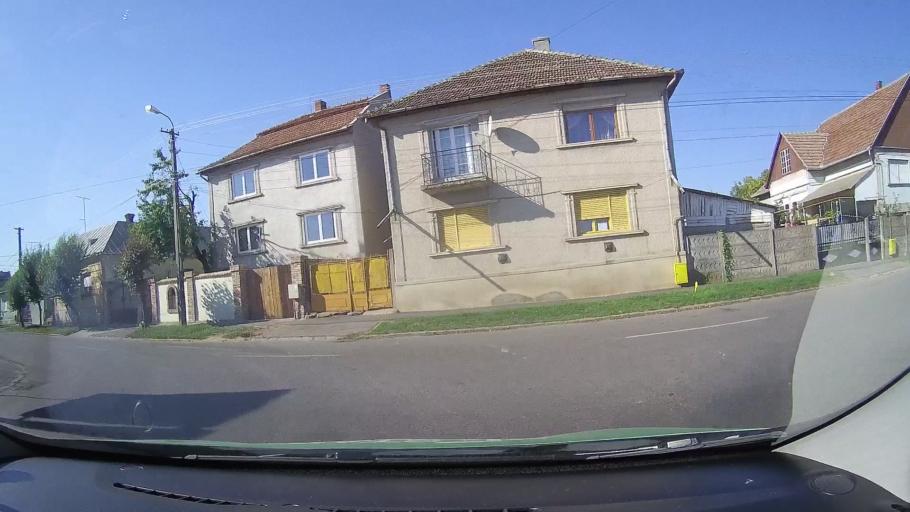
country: RO
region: Satu Mare
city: Carei
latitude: 47.6787
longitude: 22.4637
